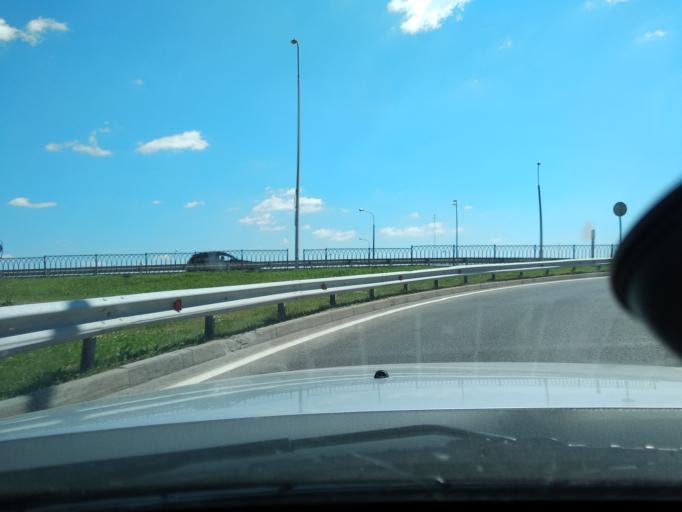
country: RU
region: Tatarstan
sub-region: Gorod Kazan'
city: Kazan
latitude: 55.8262
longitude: 49.1593
